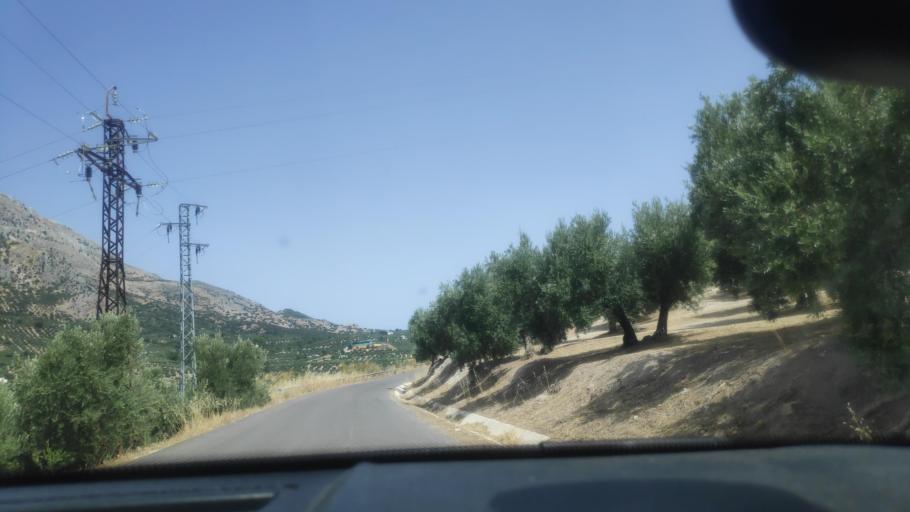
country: ES
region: Andalusia
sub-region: Provincia de Jaen
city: Jimena
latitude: 37.7988
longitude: -3.4496
